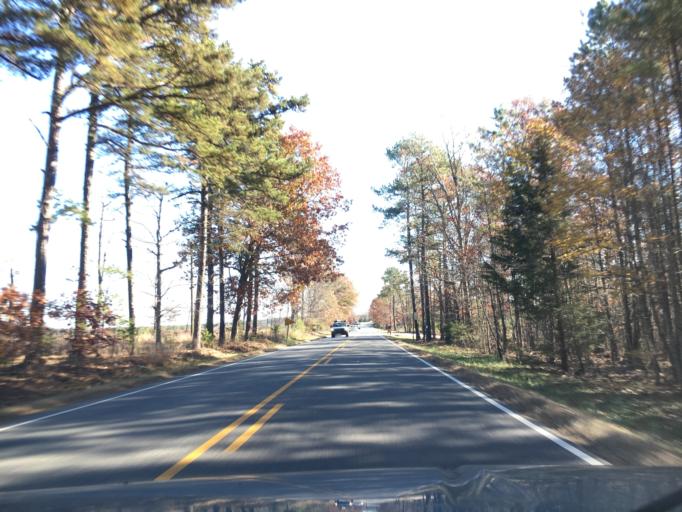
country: US
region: Virginia
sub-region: Appomattox County
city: Appomattox
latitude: 37.4561
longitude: -78.6954
